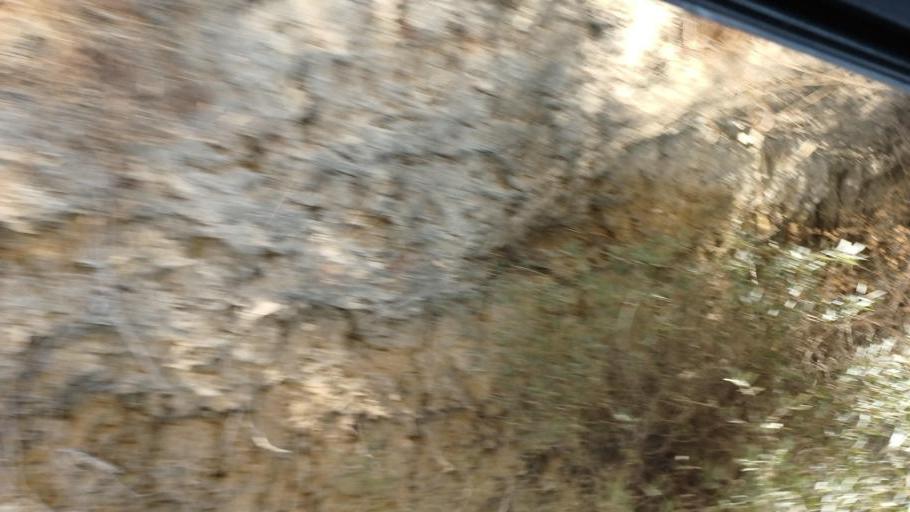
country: CY
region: Pafos
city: Tala
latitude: 34.9350
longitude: 32.4799
